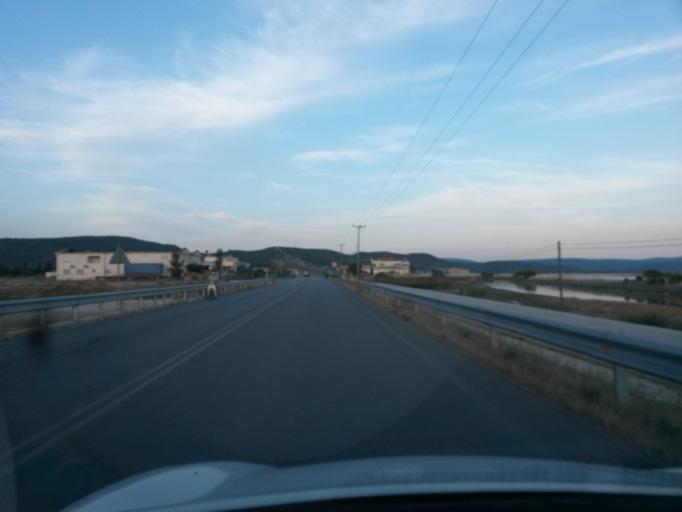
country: GR
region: North Aegean
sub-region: Nomos Lesvou
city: Kalloni
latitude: 39.2257
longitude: 26.2434
